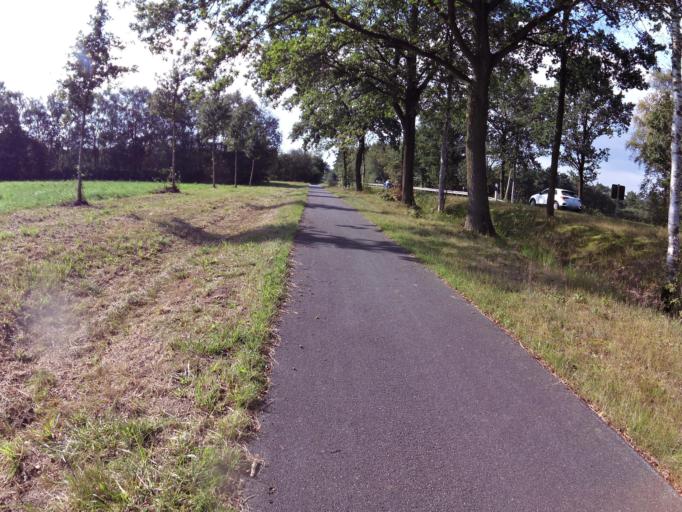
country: DE
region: Lower Saxony
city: Bremervorde
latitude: 53.4647
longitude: 9.1413
